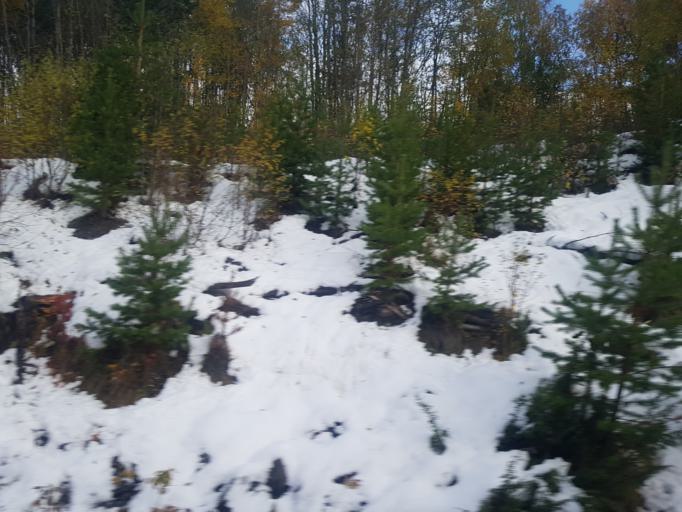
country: NO
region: Oppland
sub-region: Dovre
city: Dombas
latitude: 62.0857
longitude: 9.1247
